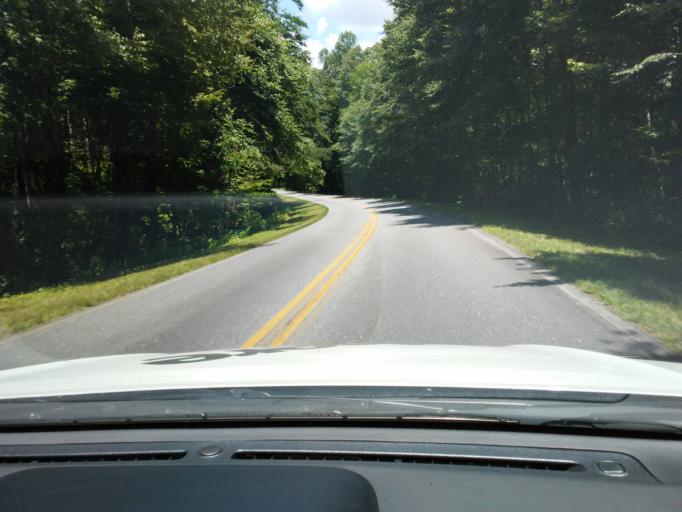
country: US
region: Georgia
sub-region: Towns County
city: Hiawassee
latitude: 34.8638
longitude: -83.7658
